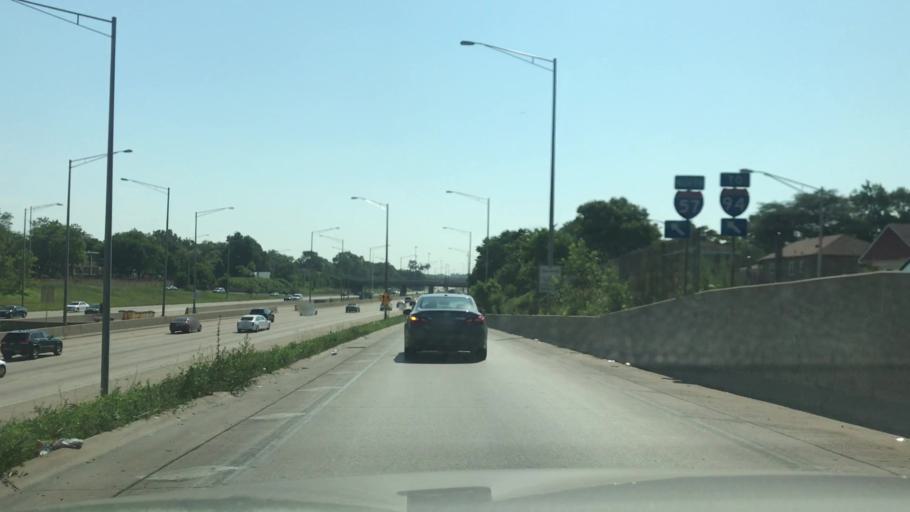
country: US
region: Illinois
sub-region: Cook County
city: Calumet Park
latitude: 41.7143
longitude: -87.6420
